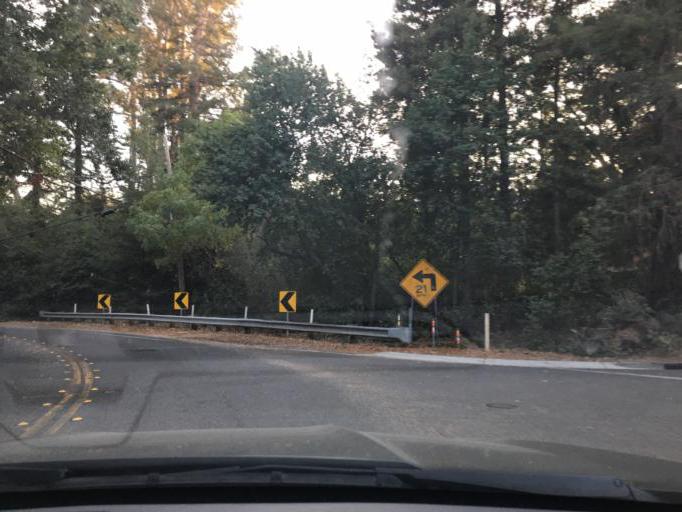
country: US
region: California
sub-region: Santa Clara County
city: Monte Sereno
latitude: 37.2568
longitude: -121.9934
